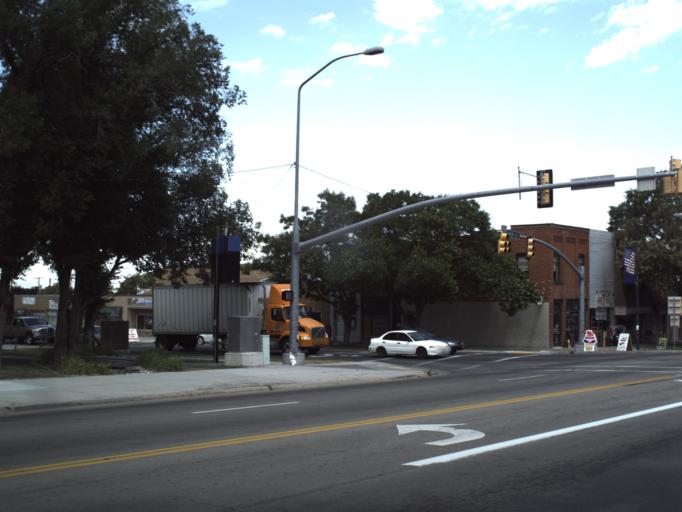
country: US
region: Utah
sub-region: Tooele County
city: Tooele
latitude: 40.5272
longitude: -112.2985
